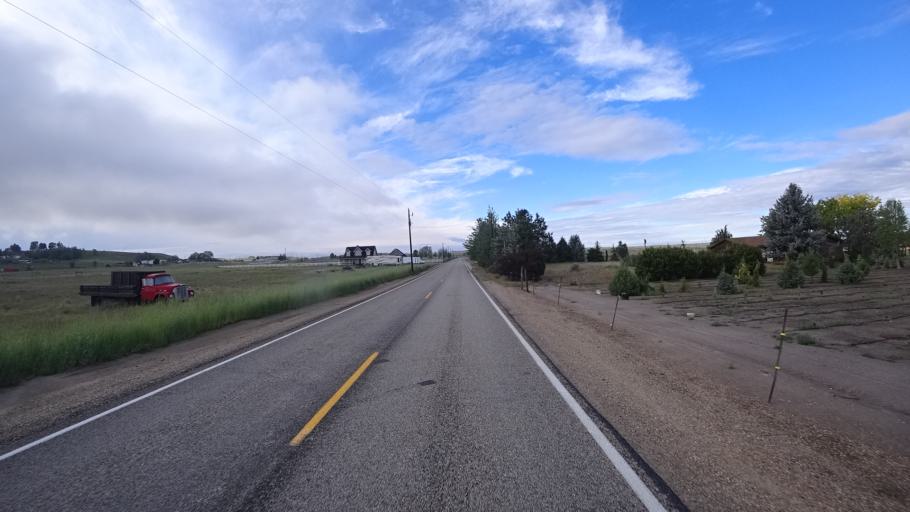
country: US
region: Idaho
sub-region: Ada County
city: Star
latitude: 43.7763
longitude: -116.4732
